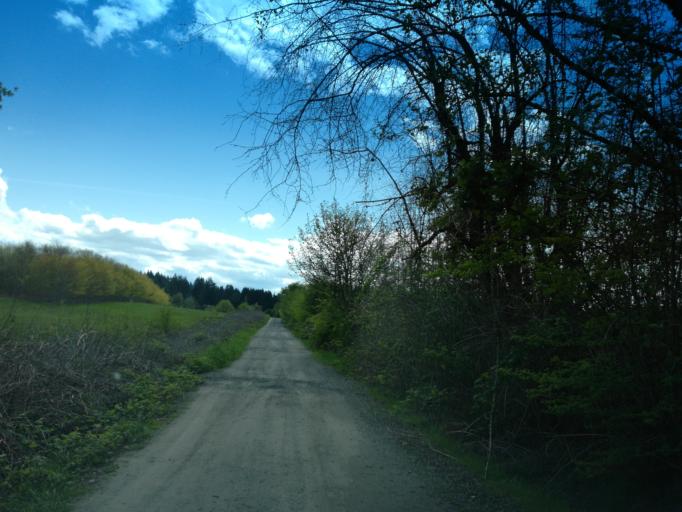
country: US
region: Oregon
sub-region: Clackamas County
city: Damascus
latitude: 45.4536
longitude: -122.4476
